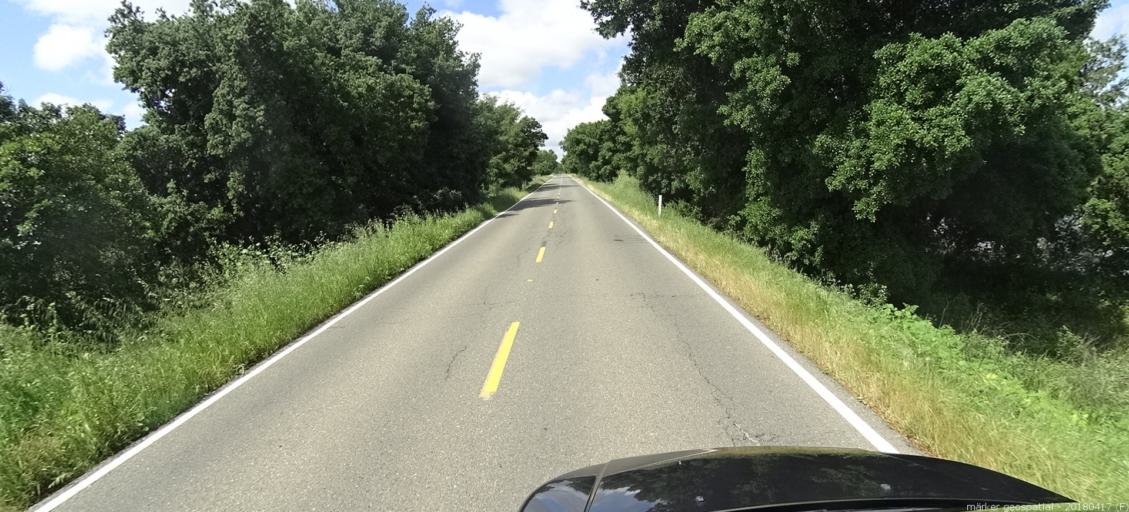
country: US
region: California
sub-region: Sacramento County
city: Walnut Grove
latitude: 38.2386
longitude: -121.5229
